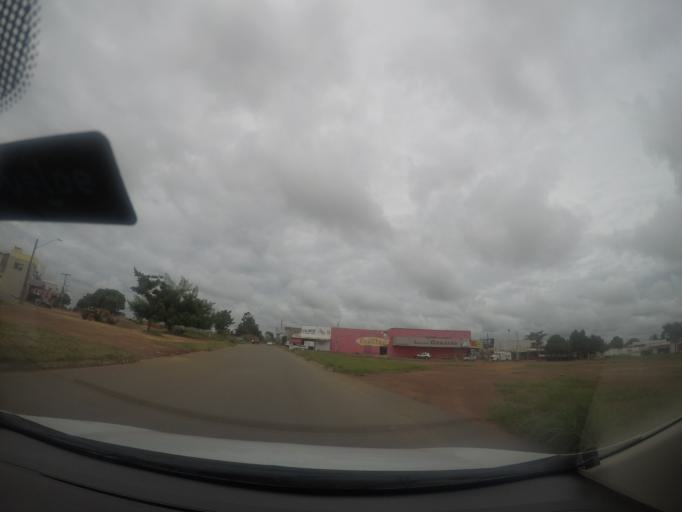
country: BR
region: Goias
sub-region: Trindade
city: Trindade
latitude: -16.6903
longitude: -49.4056
